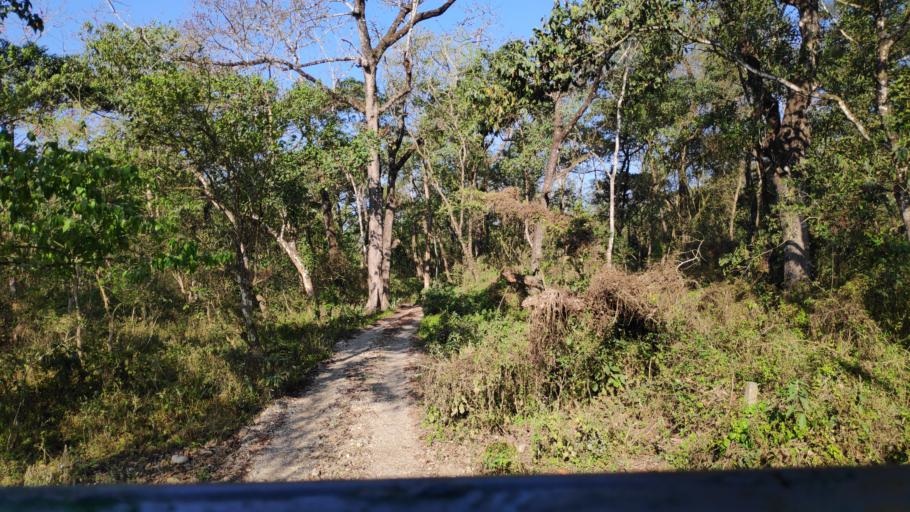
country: NP
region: Central Region
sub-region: Narayani Zone
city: Bharatpur
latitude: 27.5595
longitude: 84.5426
